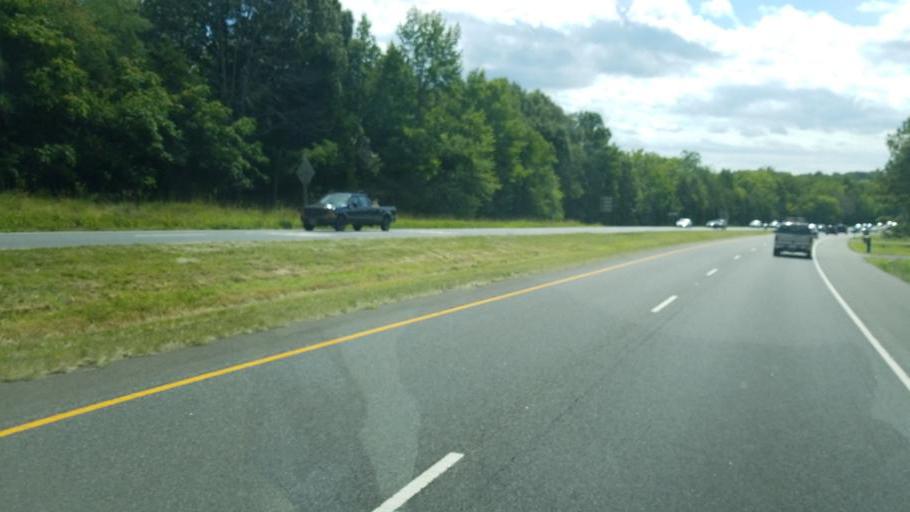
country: US
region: Virginia
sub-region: Stafford County
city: Falmouth
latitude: 38.3993
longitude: -77.5618
